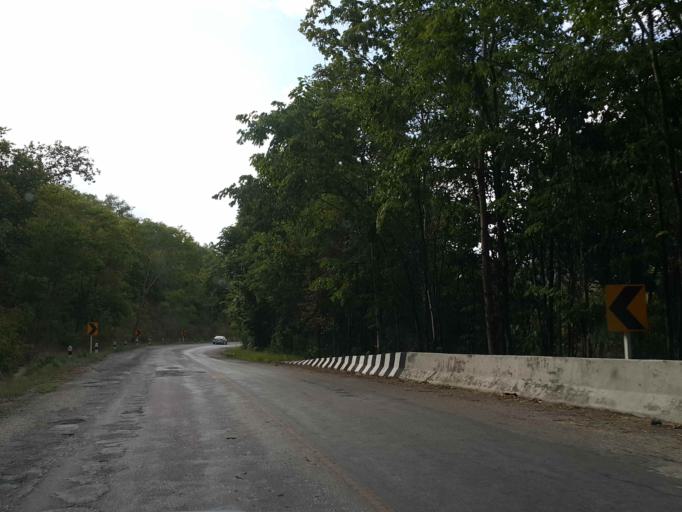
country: TH
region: Lampang
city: Thoen
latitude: 17.6266
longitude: 99.3127
